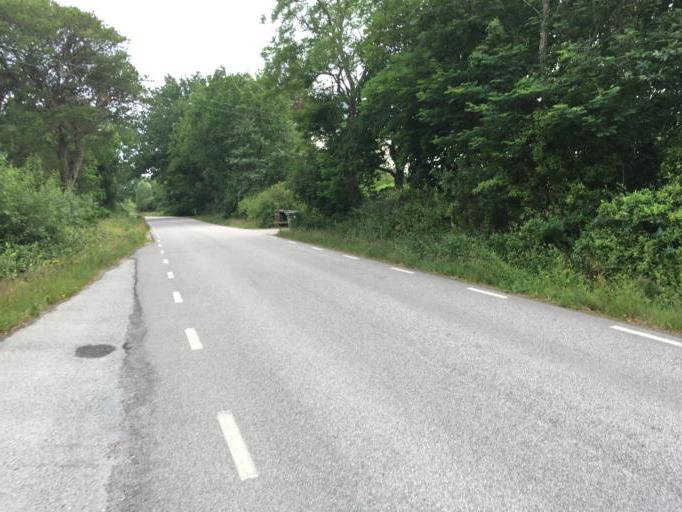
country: SE
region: Blekinge
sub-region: Karlskrona Kommun
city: Sturko
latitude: 56.0945
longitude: 15.6942
